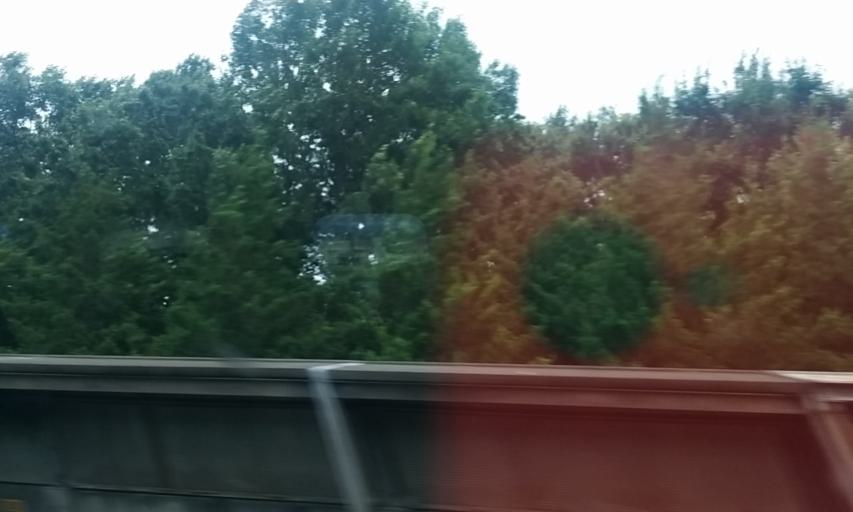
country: JP
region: Tochigi
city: Oyama
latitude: 36.2637
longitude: 139.7720
